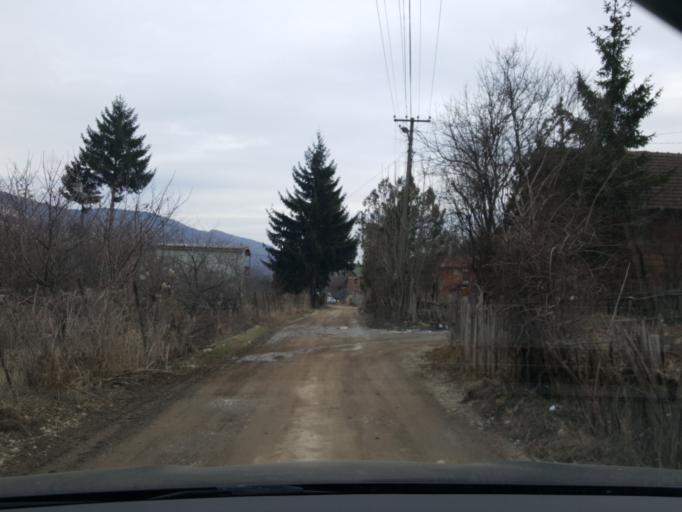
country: RS
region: Central Serbia
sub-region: Pirotski Okrug
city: Dimitrovgrad
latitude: 43.0065
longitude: 22.7557
